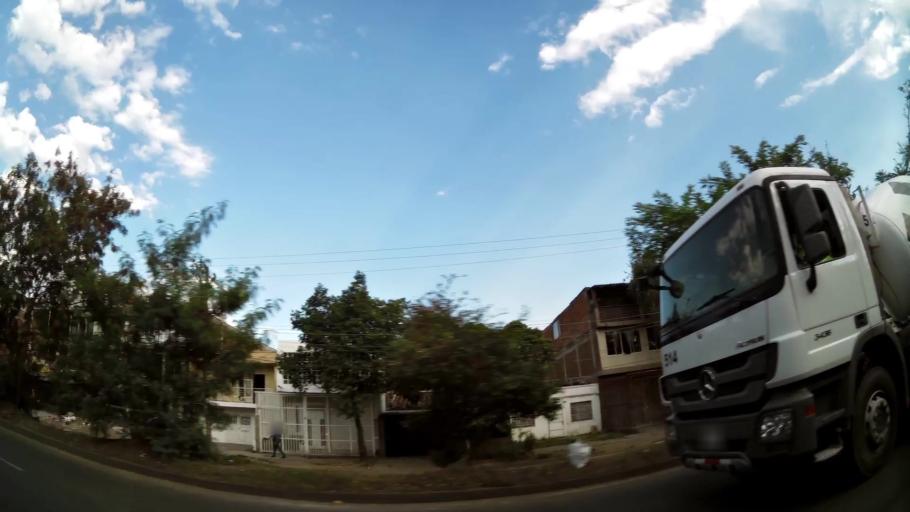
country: CO
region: Valle del Cauca
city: Cali
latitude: 3.4466
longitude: -76.4891
